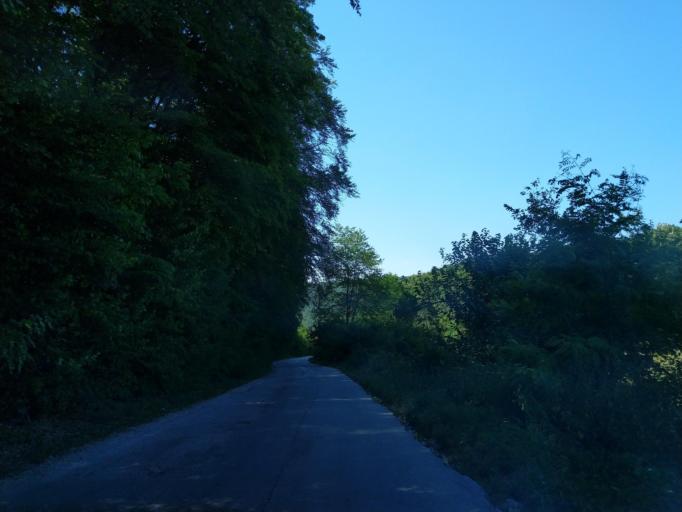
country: RS
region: Central Serbia
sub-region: Zlatiborski Okrug
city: Uzice
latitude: 43.8245
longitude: 19.8566
